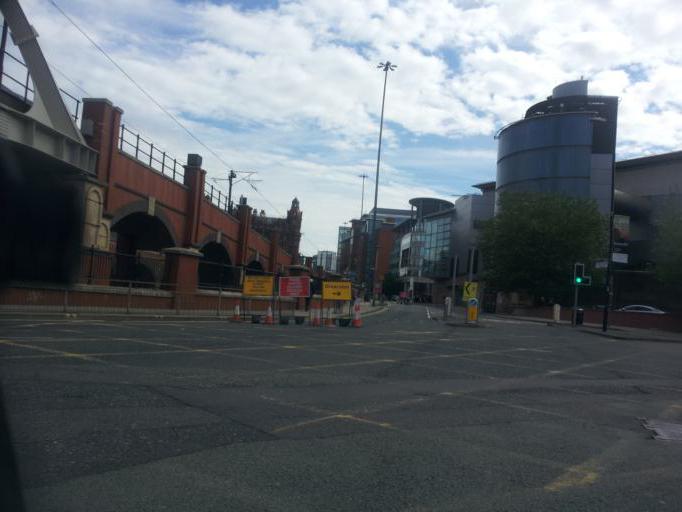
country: GB
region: England
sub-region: Manchester
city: Hulme
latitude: 53.4751
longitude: -2.2476
